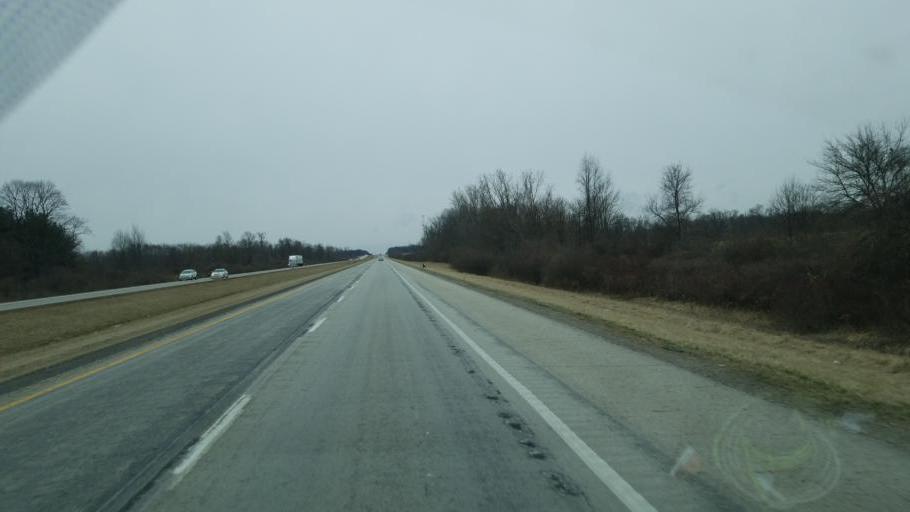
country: US
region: Indiana
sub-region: Marshall County
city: Argos
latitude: 41.1551
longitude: -86.2400
